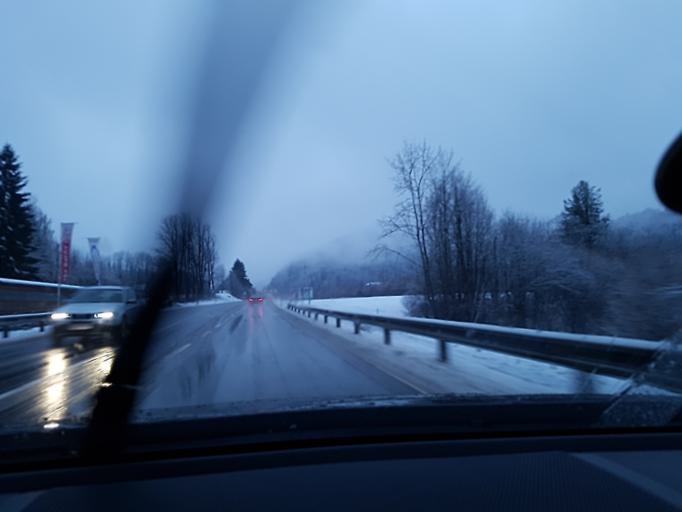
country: AT
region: Upper Austria
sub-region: Politischer Bezirk Gmunden
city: Bad Goisern
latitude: 47.6685
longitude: 13.6100
